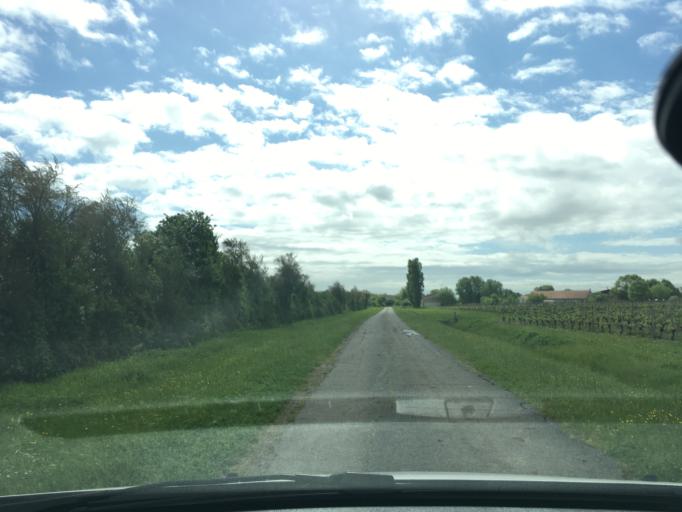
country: FR
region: Aquitaine
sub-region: Departement de la Gironde
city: Saint-Estephe
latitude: 45.3260
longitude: -0.8028
